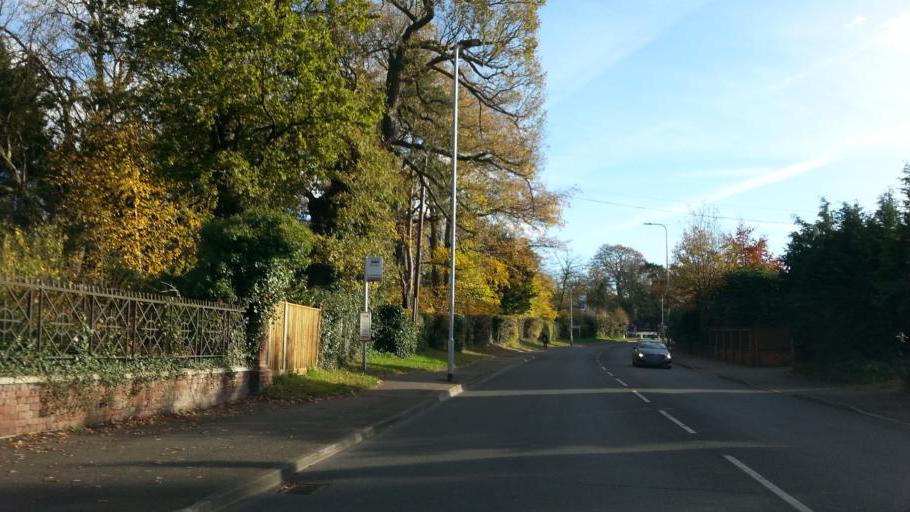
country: GB
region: England
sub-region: Reading
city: Reading
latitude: 51.4404
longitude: -0.9520
